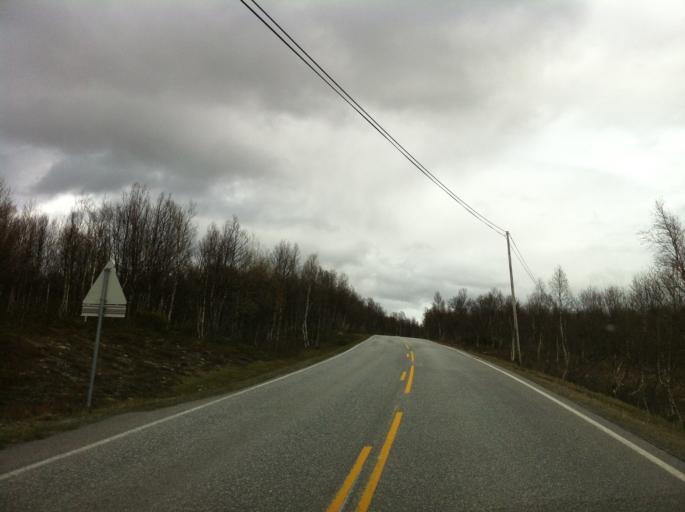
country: NO
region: Sor-Trondelag
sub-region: Roros
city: Roros
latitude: 62.6126
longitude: 11.6031
